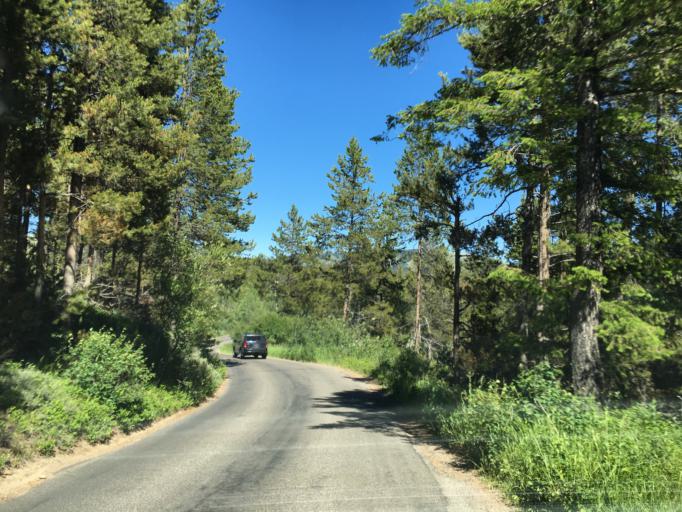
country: US
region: Wyoming
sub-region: Teton County
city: Moose Wilson Road
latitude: 43.6311
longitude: -110.7749
